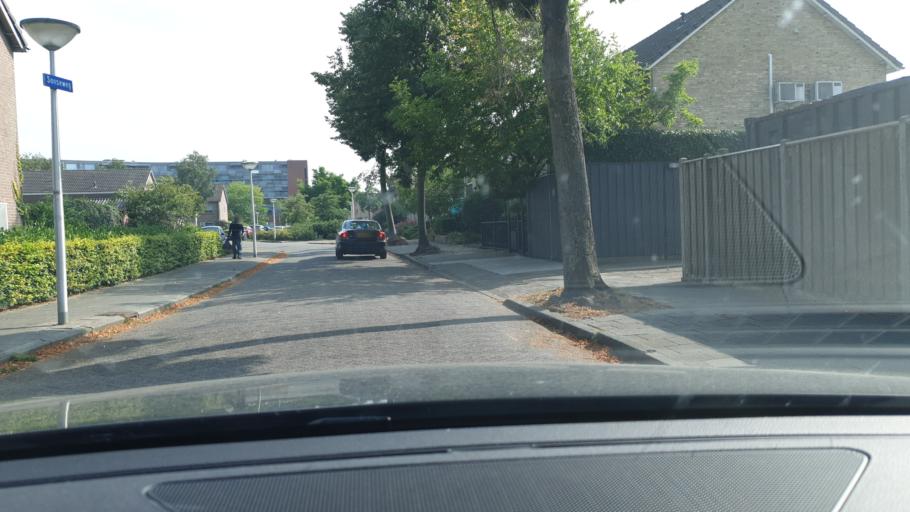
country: NL
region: North Brabant
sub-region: Gemeente Son en Breugel
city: Son
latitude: 51.4789
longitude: 5.4951
